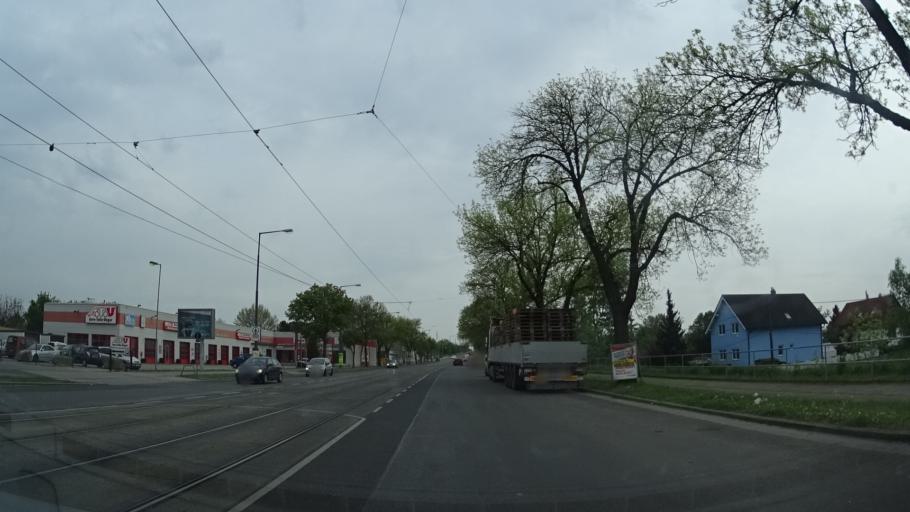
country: AT
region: Lower Austria
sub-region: Politischer Bezirk Korneuburg
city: Langenzersdorf
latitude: 48.2866
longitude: 16.3837
